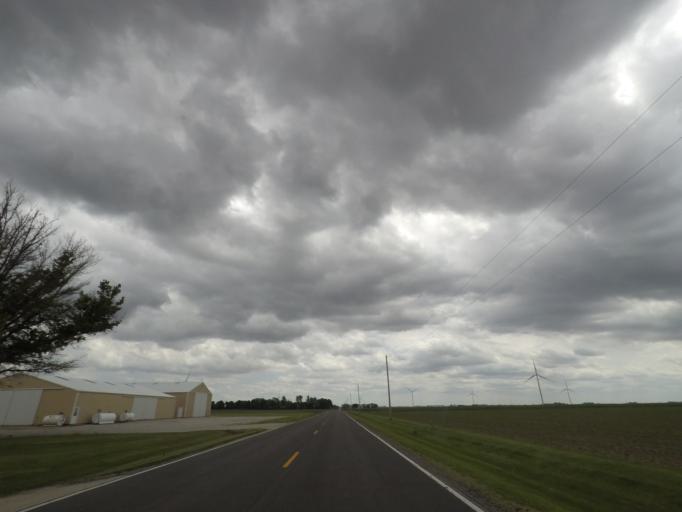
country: US
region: Illinois
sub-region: Macon County
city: Warrensburg
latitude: 39.9928
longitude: -89.0856
